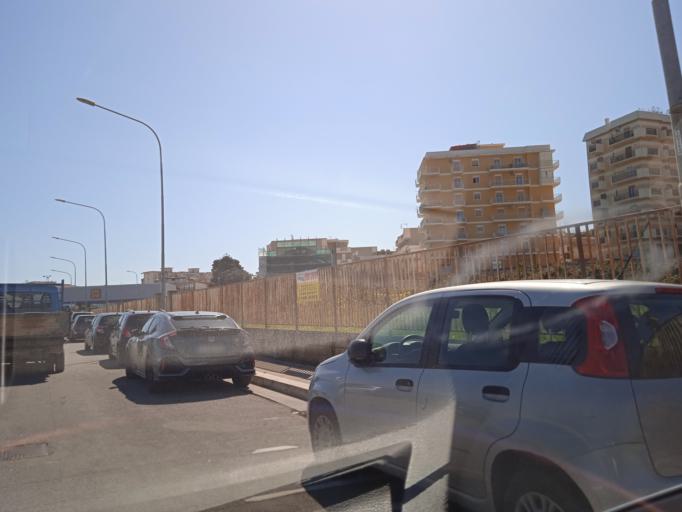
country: IT
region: Sicily
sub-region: Palermo
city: Villabate
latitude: 38.0773
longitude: 13.4492
